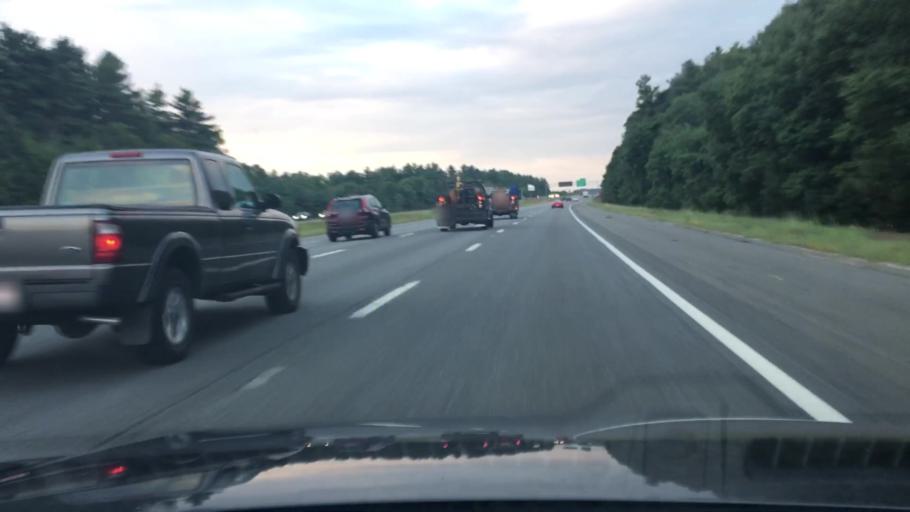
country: US
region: Massachusetts
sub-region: Essex County
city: Topsfield
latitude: 42.6393
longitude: -70.9772
